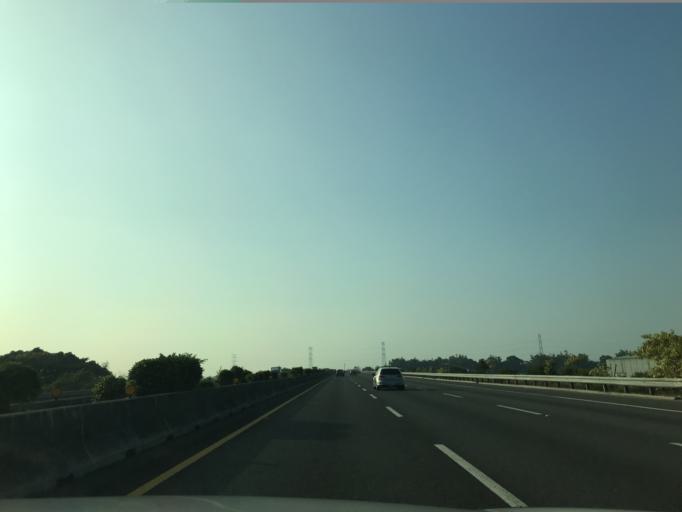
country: TW
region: Taiwan
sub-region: Yunlin
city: Douliu
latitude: 23.8302
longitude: 120.4849
